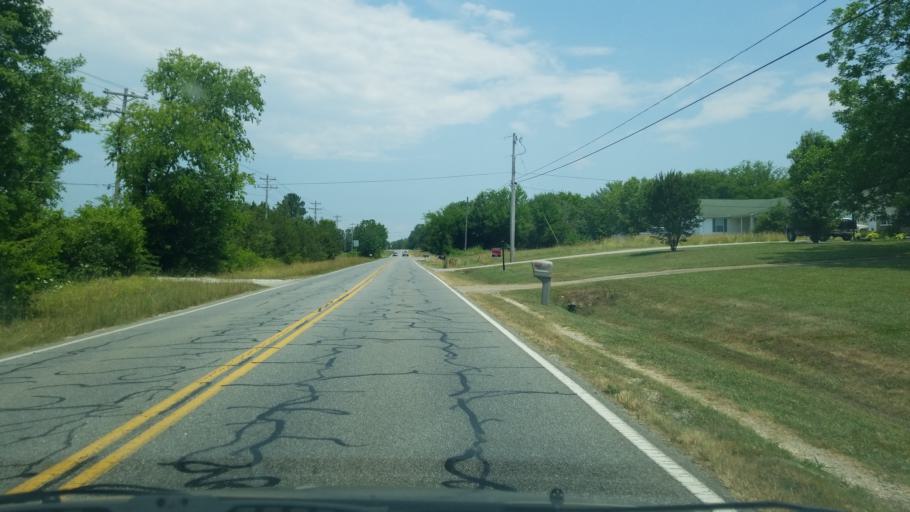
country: US
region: Tennessee
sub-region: Hamilton County
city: East Brainerd
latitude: 34.9804
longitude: -85.0973
